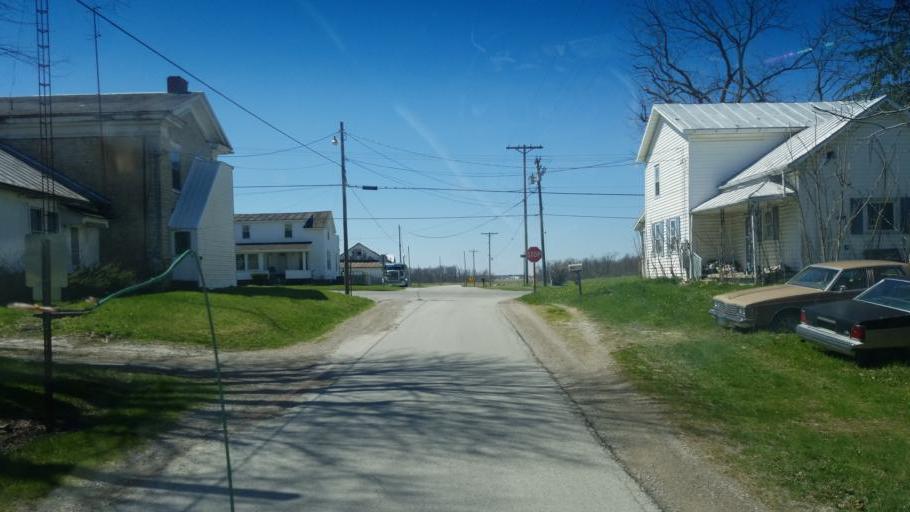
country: US
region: Ohio
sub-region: Huron County
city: Willard
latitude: 41.0521
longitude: -82.8930
